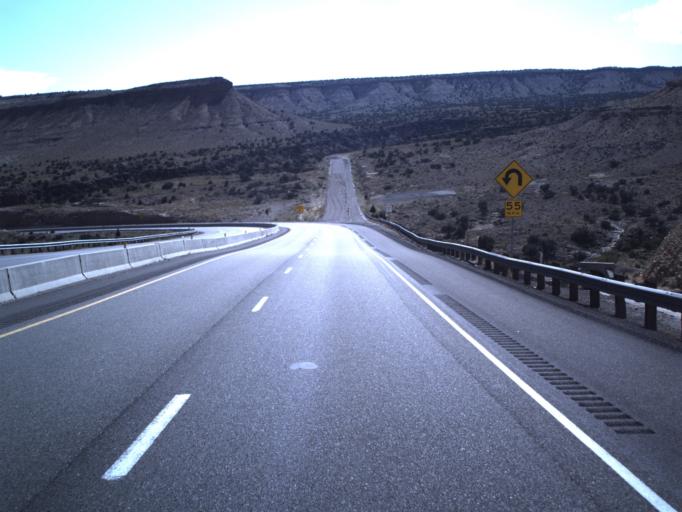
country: US
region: Utah
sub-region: Carbon County
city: East Carbon City
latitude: 38.9336
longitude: -110.4641
